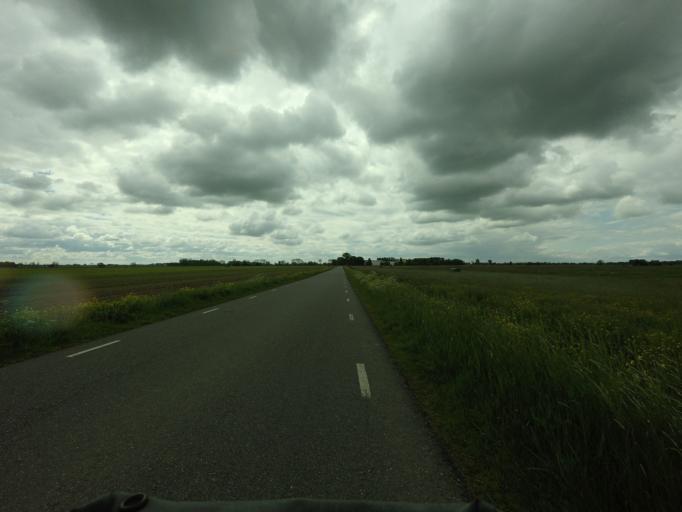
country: NL
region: Utrecht
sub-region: Gemeente Lopik
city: Lopik
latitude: 51.9410
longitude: 4.9348
